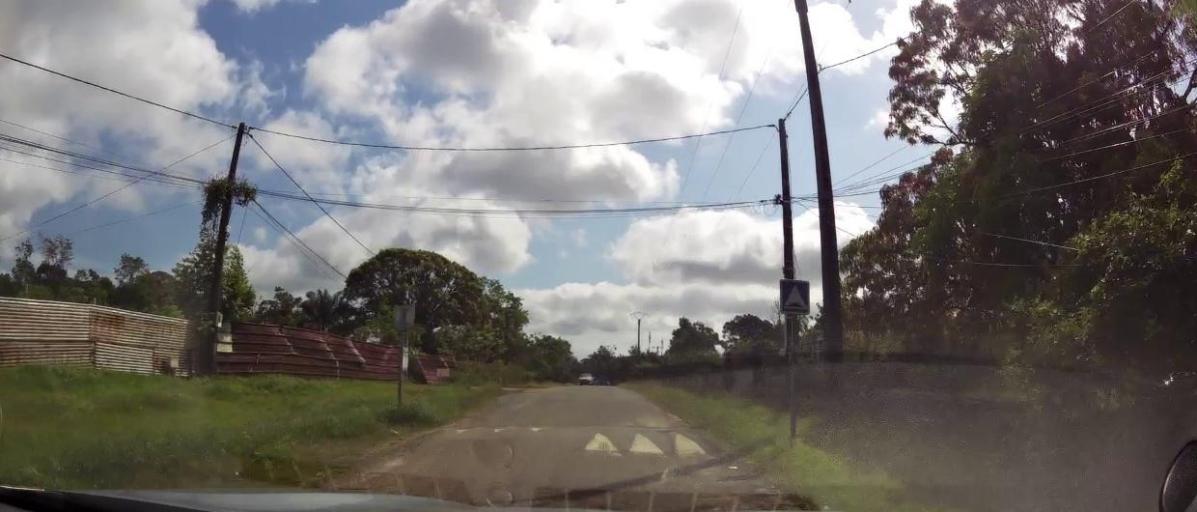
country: GF
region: Guyane
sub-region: Guyane
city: Matoury
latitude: 4.8307
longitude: -52.3108
